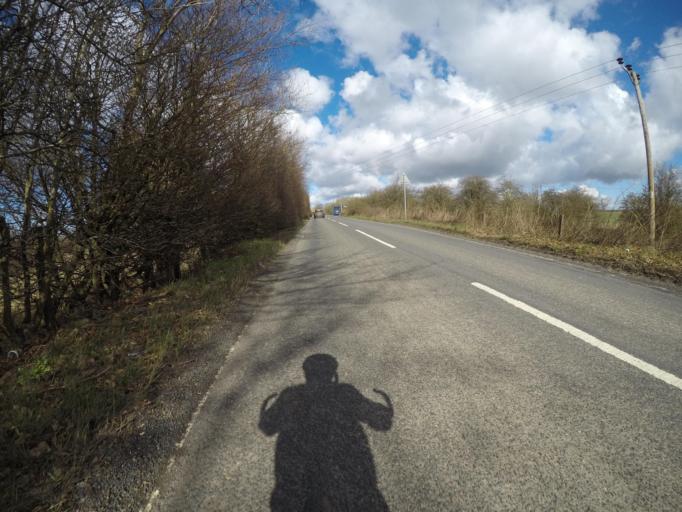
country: GB
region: Scotland
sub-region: North Ayrshire
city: Beith
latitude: 55.7342
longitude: -4.6157
